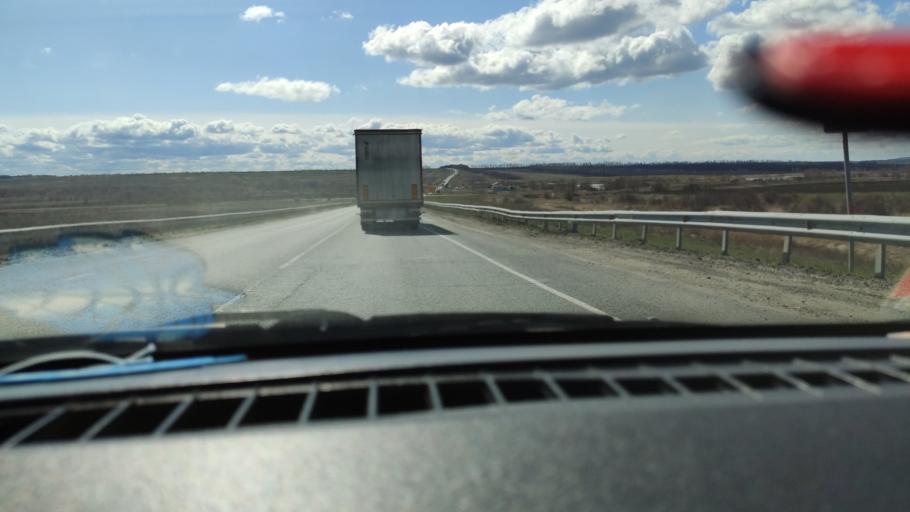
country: RU
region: Saratov
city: Dukhovnitskoye
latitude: 52.7434
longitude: 48.2525
